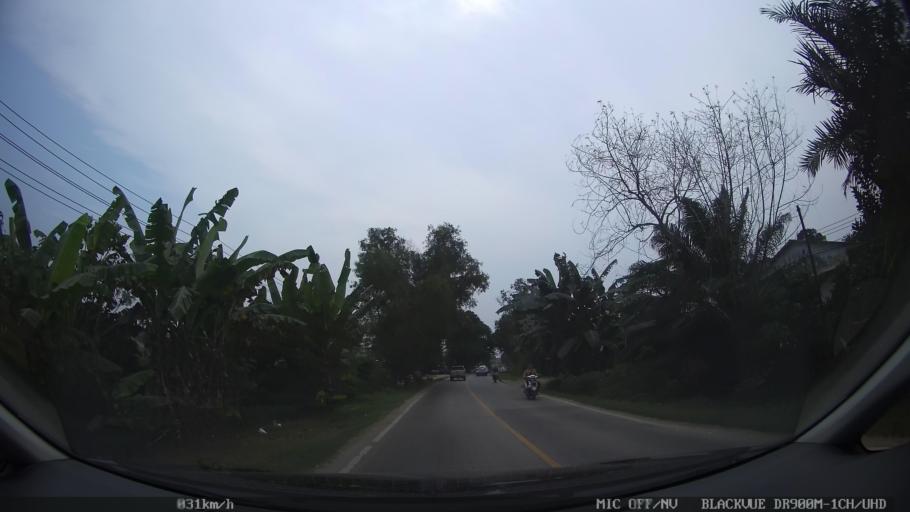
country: ID
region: Lampung
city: Panjang
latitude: -5.4028
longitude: 105.3516
